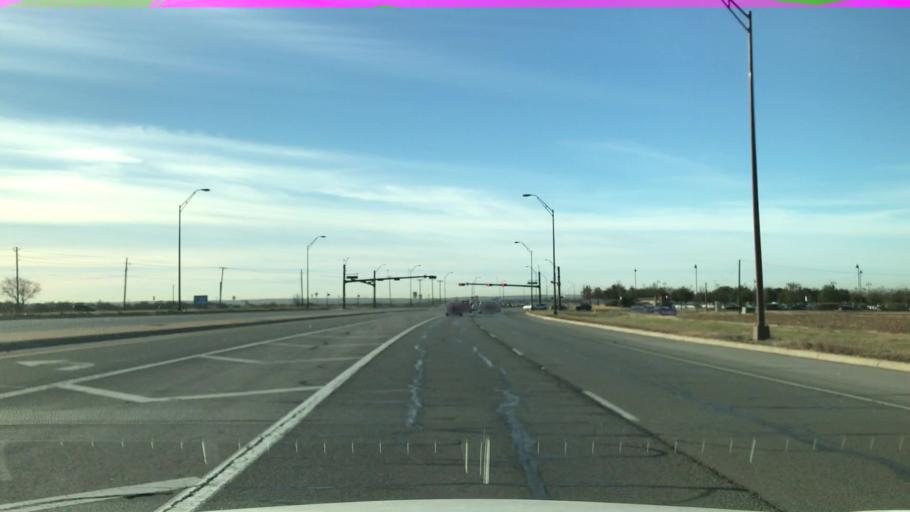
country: US
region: Texas
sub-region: Williamson County
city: Round Rock
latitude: 30.5604
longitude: -97.6460
